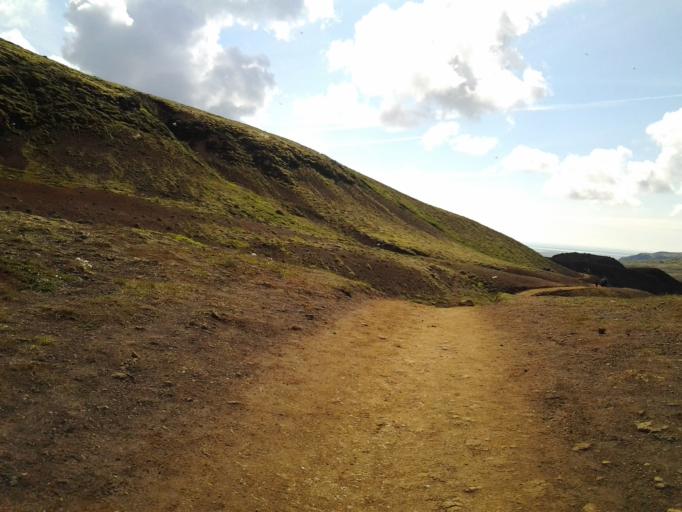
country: IS
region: South
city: Hveragerdi
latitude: 64.0366
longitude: -21.2185
